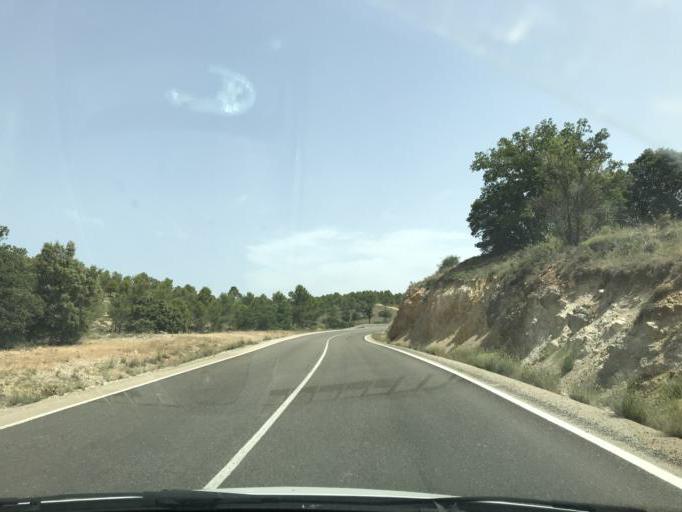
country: ES
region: Castille-La Mancha
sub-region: Provincia de Cuenca
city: Albalate de las Nogueras
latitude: 40.3932
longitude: -2.2632
